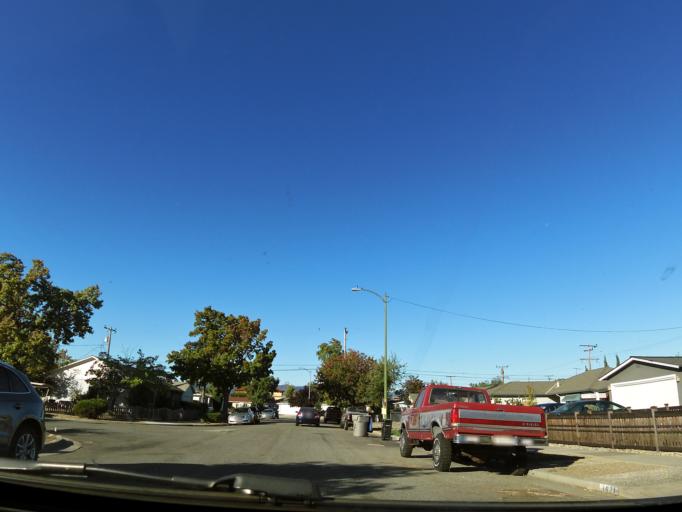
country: US
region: California
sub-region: Santa Clara County
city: Cambrian Park
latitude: 37.2706
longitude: -121.9035
